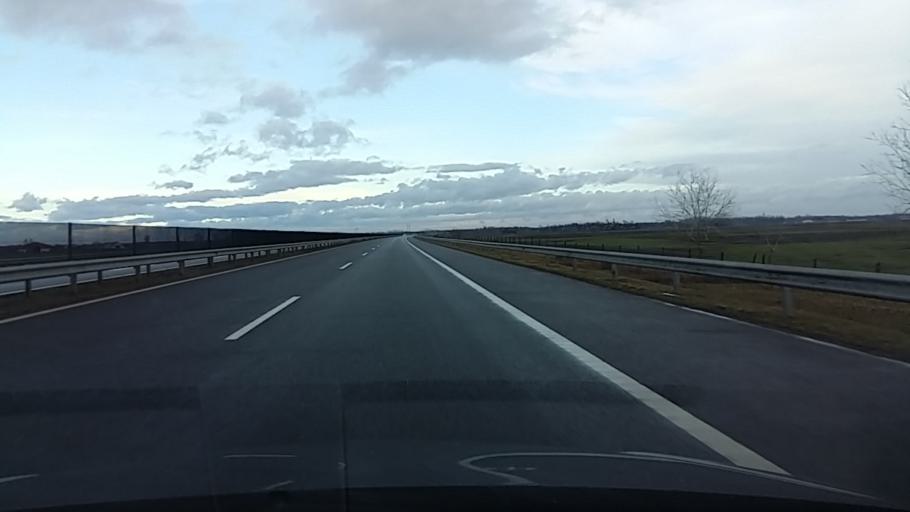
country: HU
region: Hajdu-Bihar
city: Hajdunanas
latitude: 47.8504
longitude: 21.3490
